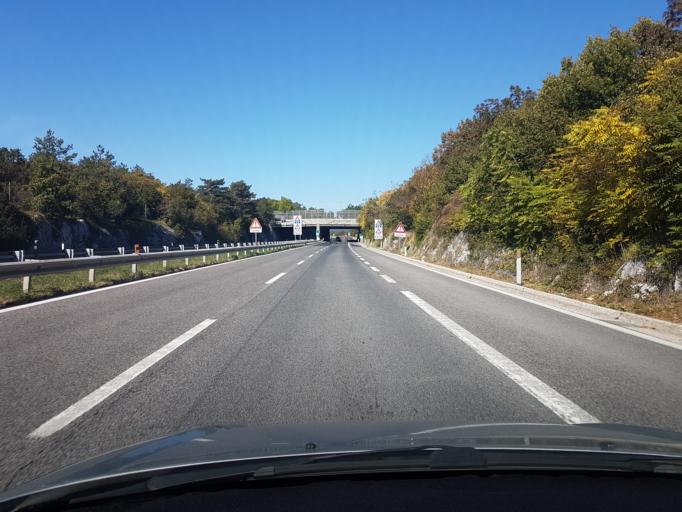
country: IT
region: Friuli Venezia Giulia
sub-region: Provincia di Trieste
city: Villa Opicina
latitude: 45.6750
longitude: 13.8191
